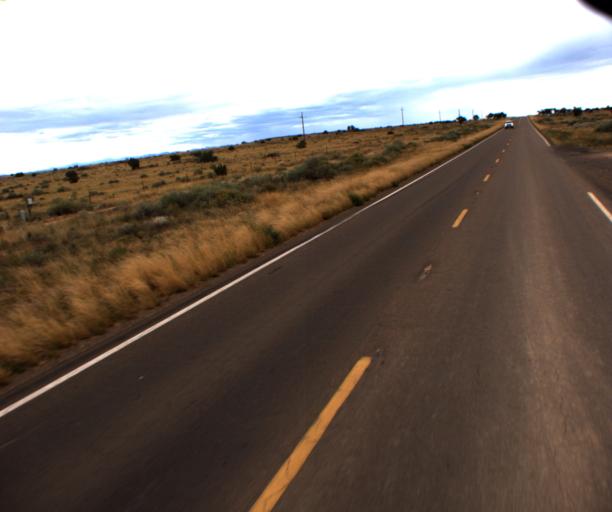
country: US
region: Arizona
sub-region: Navajo County
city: Snowflake
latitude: 34.5565
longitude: -110.0810
